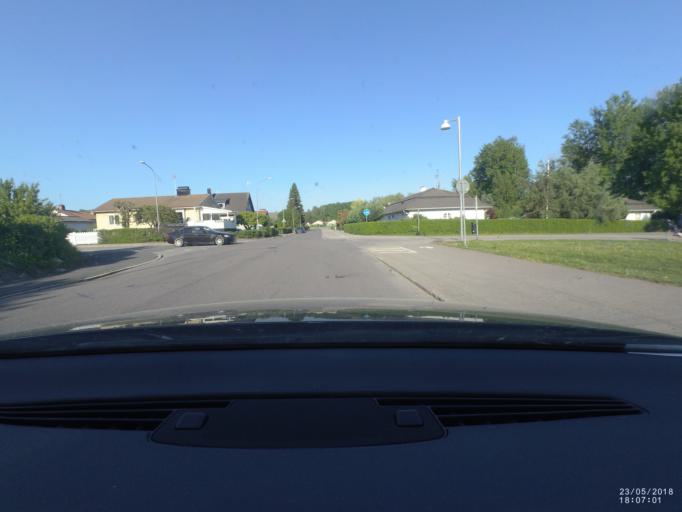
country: SE
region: Soedermanland
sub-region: Nykopings Kommun
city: Nykoping
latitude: 58.7520
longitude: 17.0325
